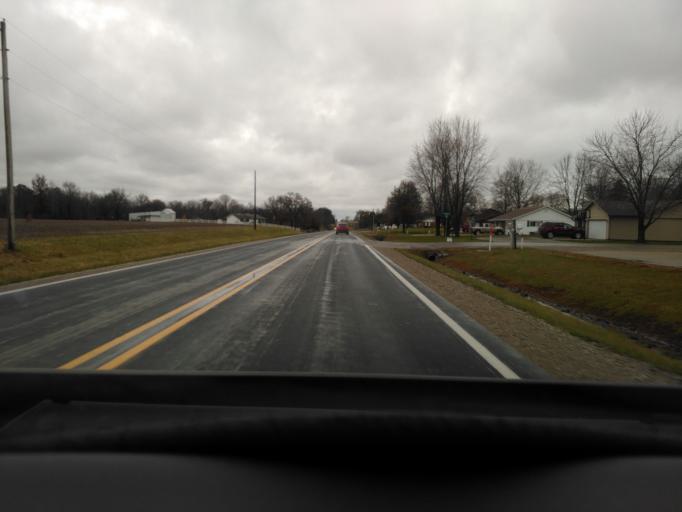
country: US
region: Illinois
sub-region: Effingham County
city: Altamont
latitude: 39.0384
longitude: -88.7482
